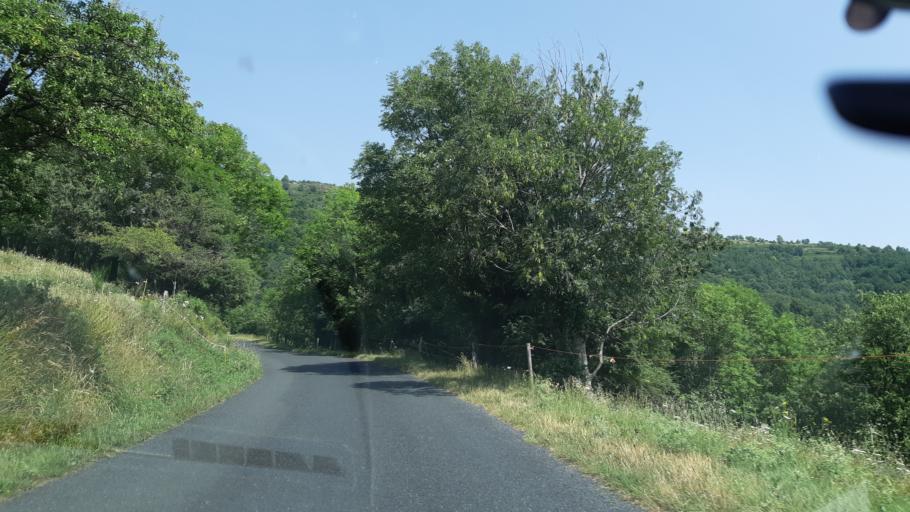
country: FR
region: Languedoc-Roussillon
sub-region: Departement des Pyrenees-Orientales
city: Arles
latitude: 42.5284
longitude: 2.6147
